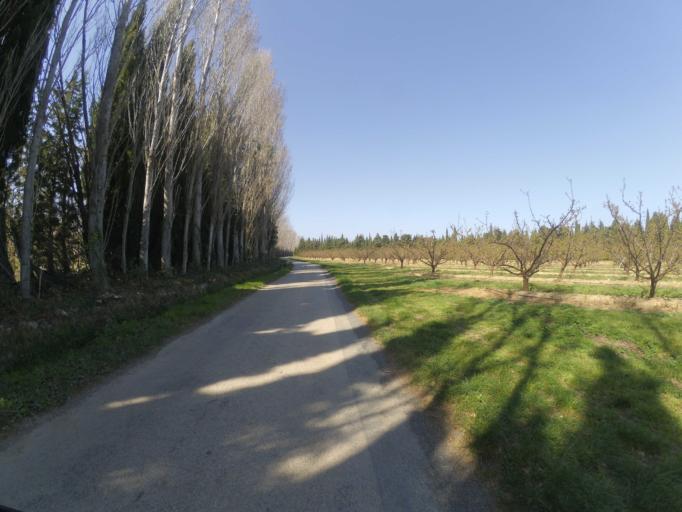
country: FR
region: Languedoc-Roussillon
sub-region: Departement des Pyrenees-Orientales
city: Pezilla-la-Riviere
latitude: 42.6734
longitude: 2.7589
